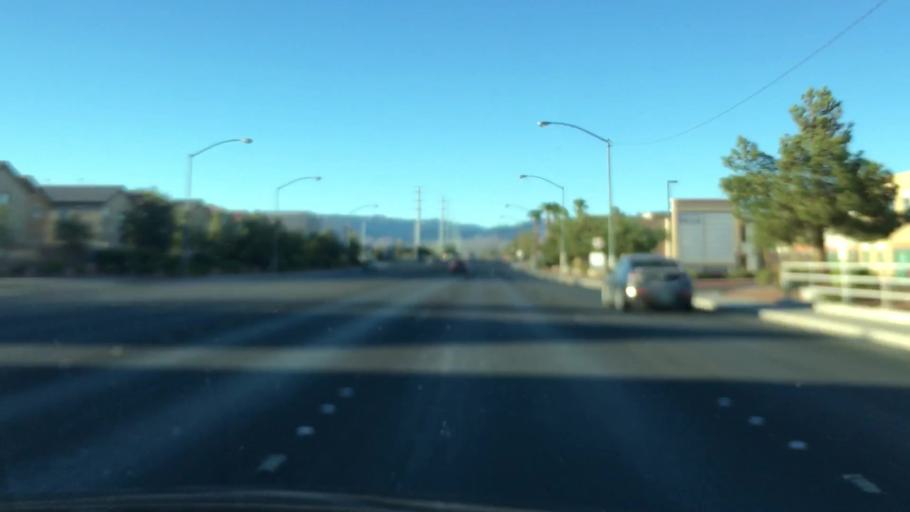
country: US
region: Nevada
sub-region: Clark County
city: Nellis Air Force Base
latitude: 36.2359
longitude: -115.0800
